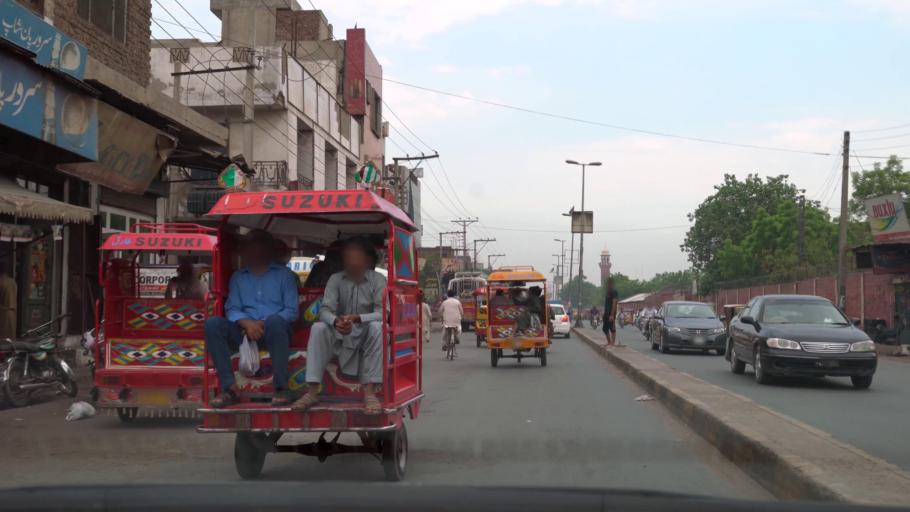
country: PK
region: Punjab
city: Faisalabad
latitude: 31.4330
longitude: 73.0917
